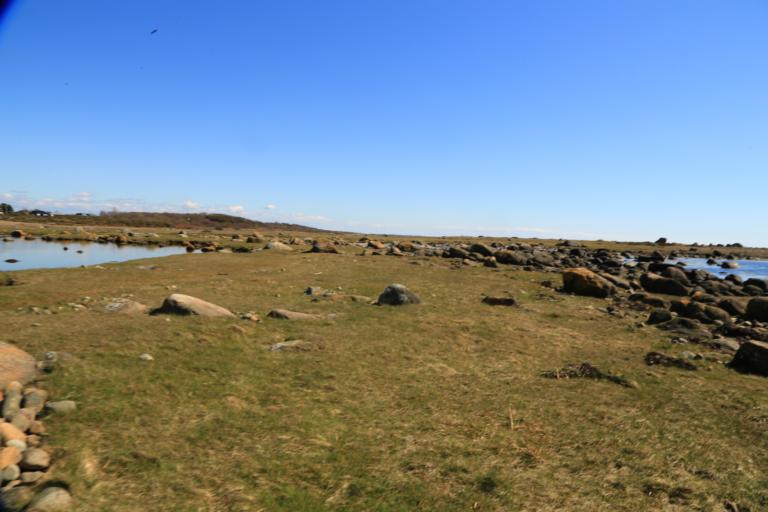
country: SE
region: Halland
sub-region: Varbergs Kommun
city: Traslovslage
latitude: 57.0428
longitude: 12.2846
